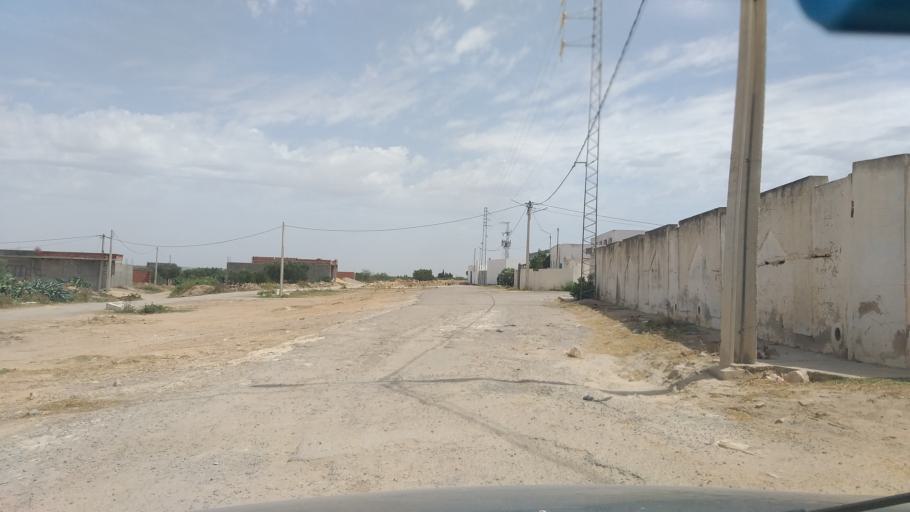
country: TN
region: Al Mahdiyah
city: El Jem
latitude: 35.3120
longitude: 10.7040
